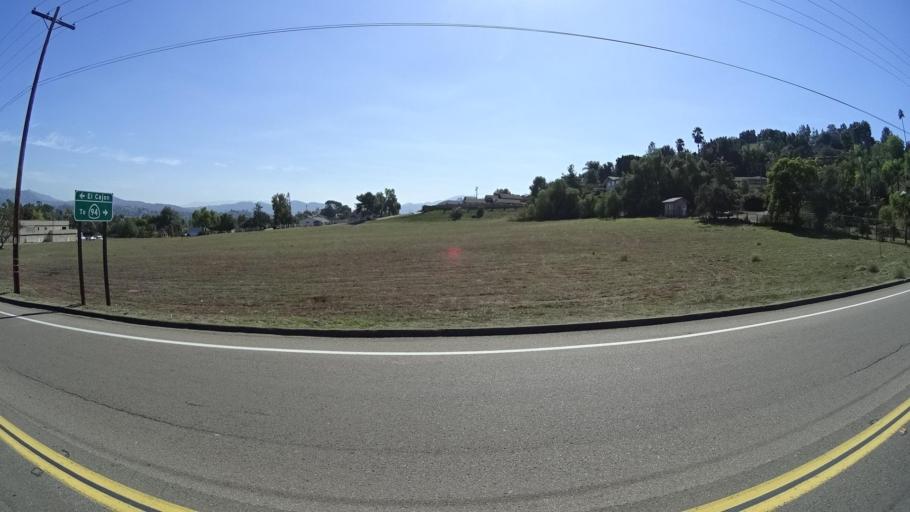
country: US
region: California
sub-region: San Diego County
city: Rancho San Diego
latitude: 32.7690
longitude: -116.9302
